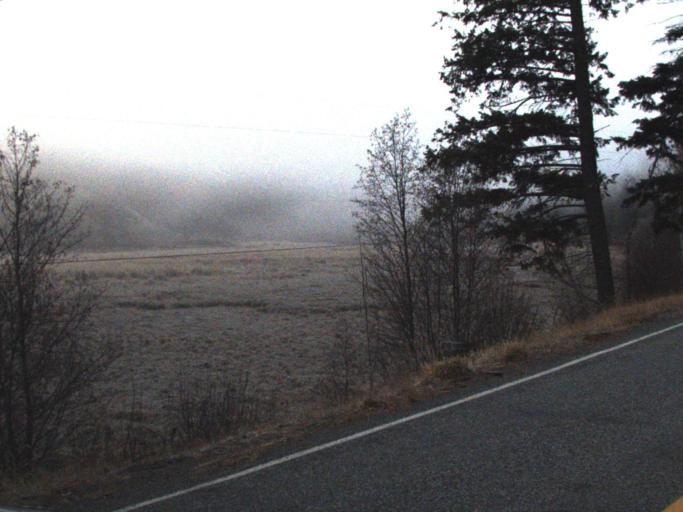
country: US
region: Washington
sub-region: Ferry County
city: Republic
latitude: 48.5668
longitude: -118.7481
